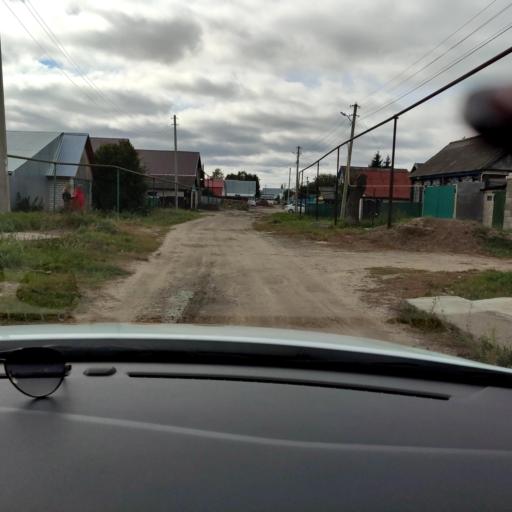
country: RU
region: Tatarstan
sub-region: Gorod Kazan'
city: Kazan
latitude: 55.7207
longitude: 49.1042
